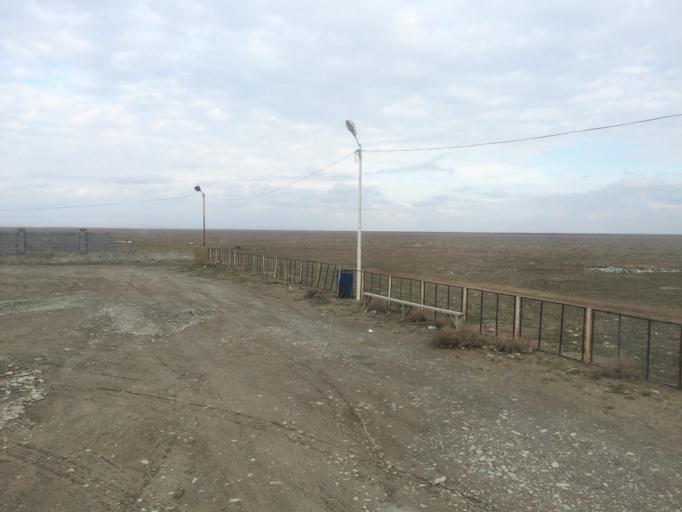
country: KZ
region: Qyzylorda
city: Shalqiya
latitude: 43.6053
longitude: 67.6735
